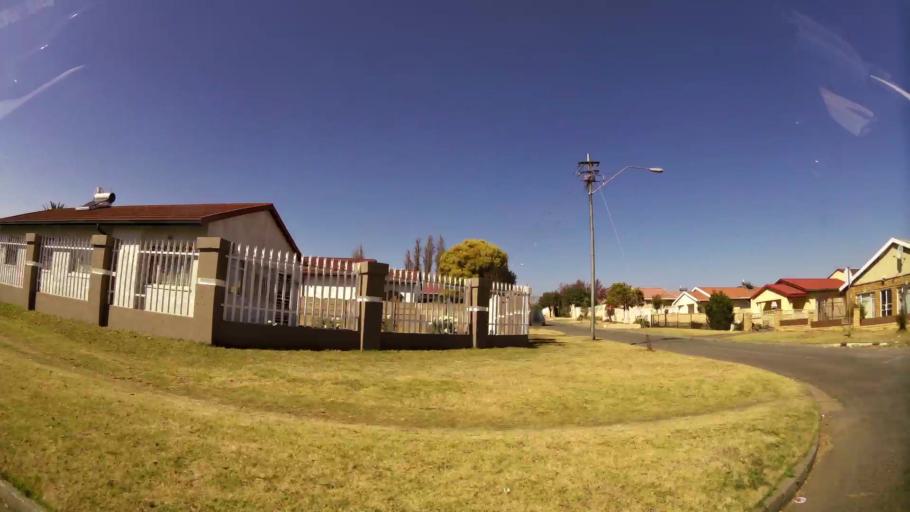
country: ZA
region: Gauteng
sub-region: City of Johannesburg Metropolitan Municipality
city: Roodepoort
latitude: -26.1952
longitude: 27.9546
